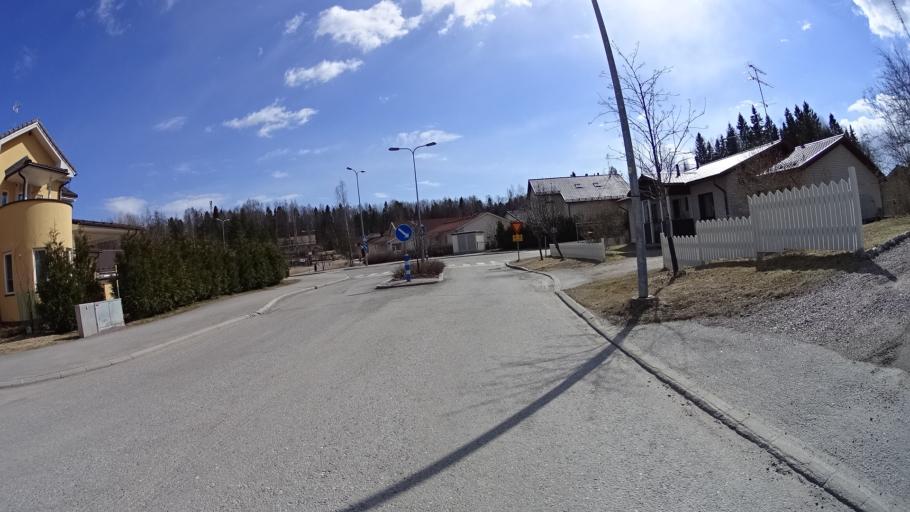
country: FI
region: Uusimaa
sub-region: Helsinki
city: Kilo
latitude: 60.2368
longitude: 24.7588
